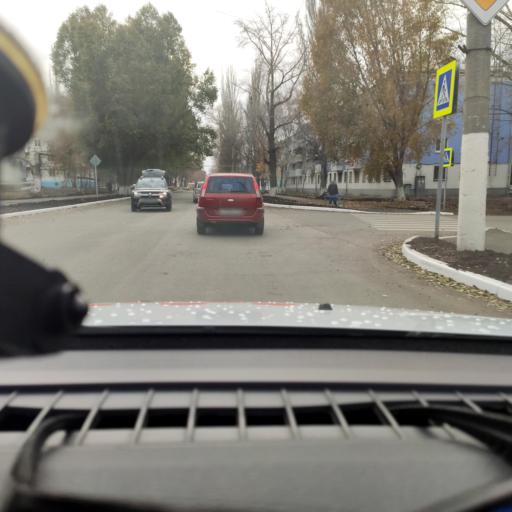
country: RU
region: Samara
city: Chapayevsk
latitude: 52.9868
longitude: 49.7223
